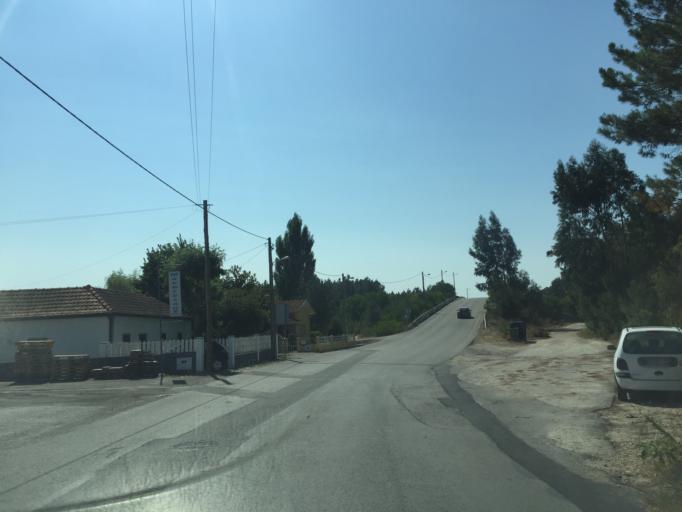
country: PT
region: Coimbra
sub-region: Montemor-O-Velho
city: Arazede
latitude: 40.3188
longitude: -8.7178
